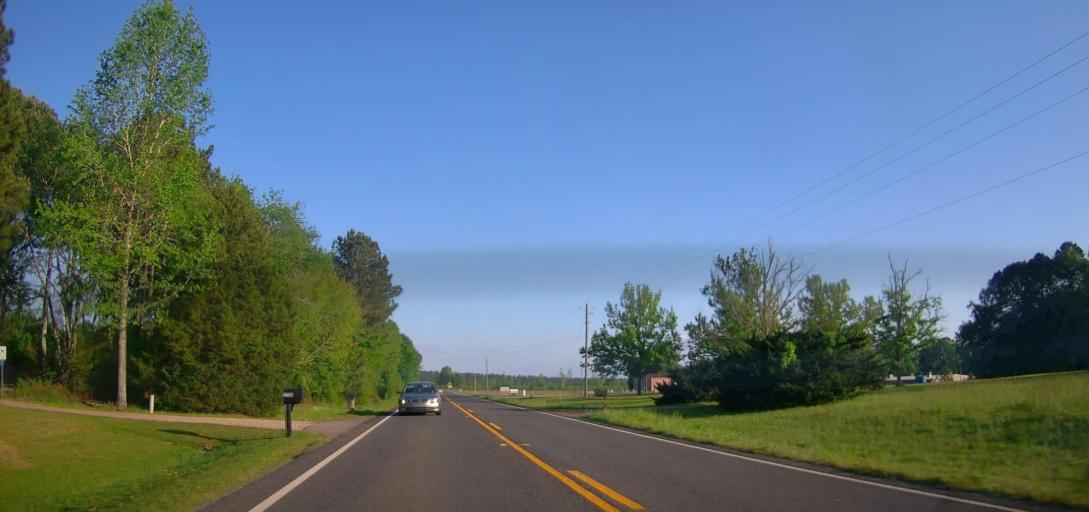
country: US
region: Georgia
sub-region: Jasper County
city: Monticello
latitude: 33.4756
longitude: -83.6427
